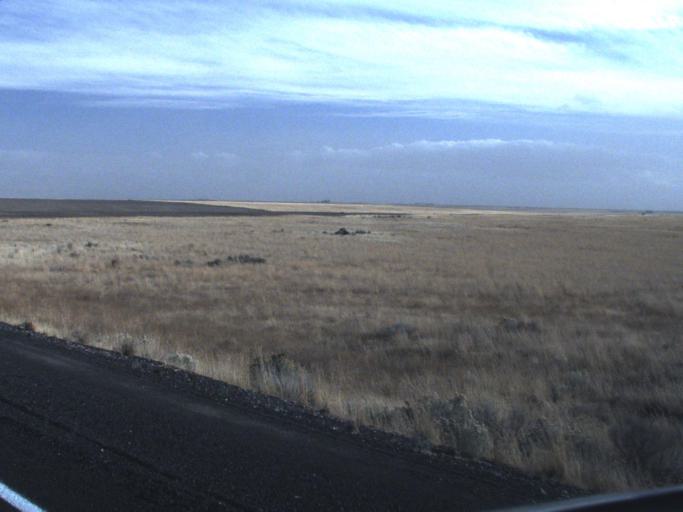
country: US
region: Washington
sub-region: Grant County
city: Moses Lake
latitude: 47.3589
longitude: -118.9596
